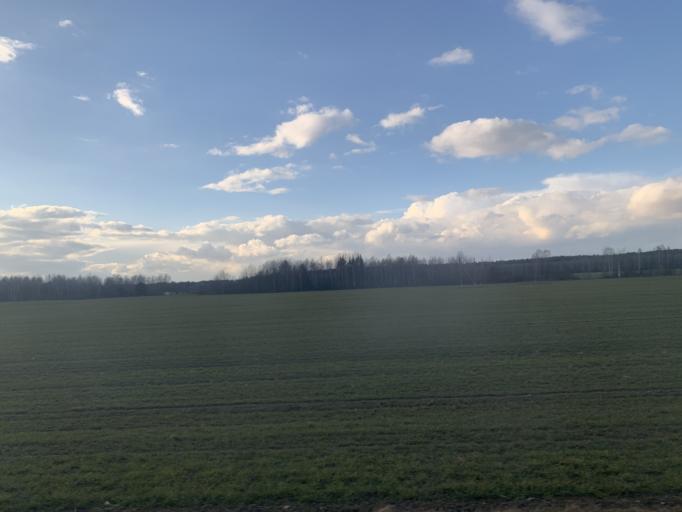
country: BY
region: Minsk
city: Novy Svyerzhan'
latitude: 53.3703
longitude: 26.7104
